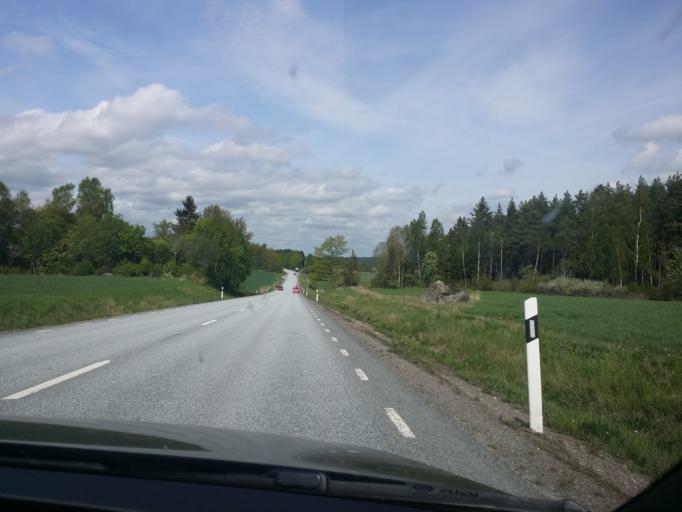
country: SE
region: Uppsala
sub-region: Habo Kommun
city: Balsta
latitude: 59.6454
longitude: 17.5667
